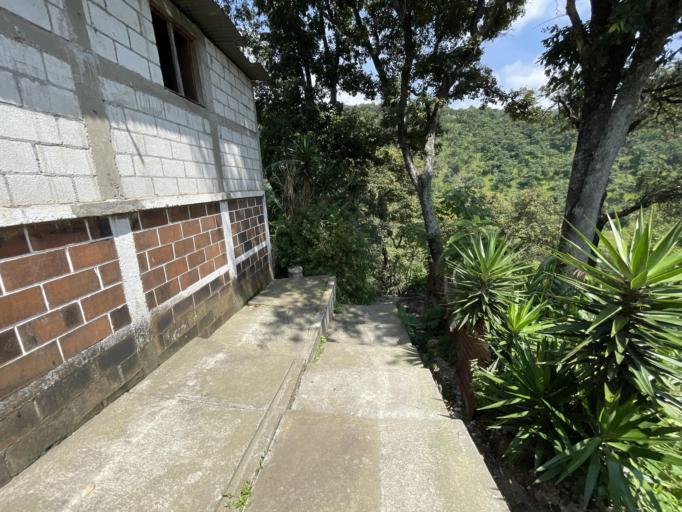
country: GT
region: Guatemala
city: Mixco
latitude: 14.6819
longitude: -90.5748
